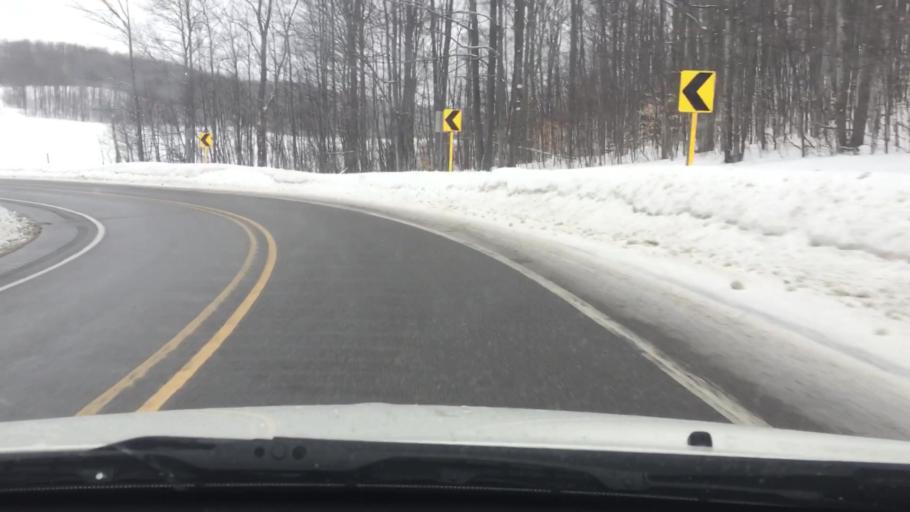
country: US
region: Michigan
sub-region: Charlevoix County
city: Boyne City
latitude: 45.0813
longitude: -84.9127
